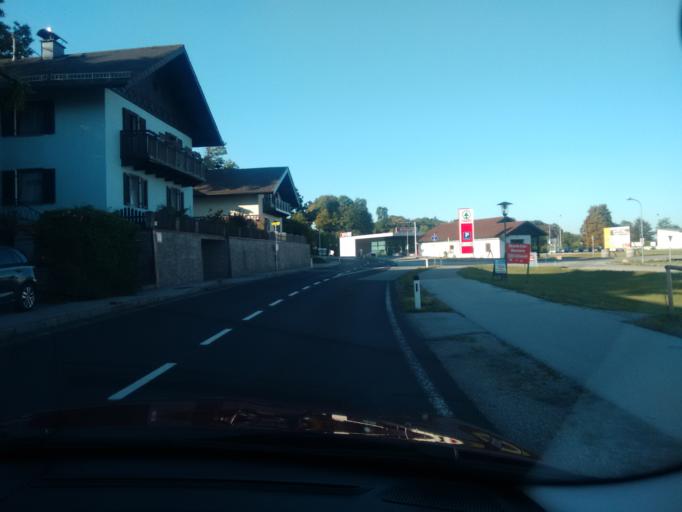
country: DE
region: Bavaria
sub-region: Upper Bavaria
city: Burghausen
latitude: 48.1583
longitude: 12.8404
